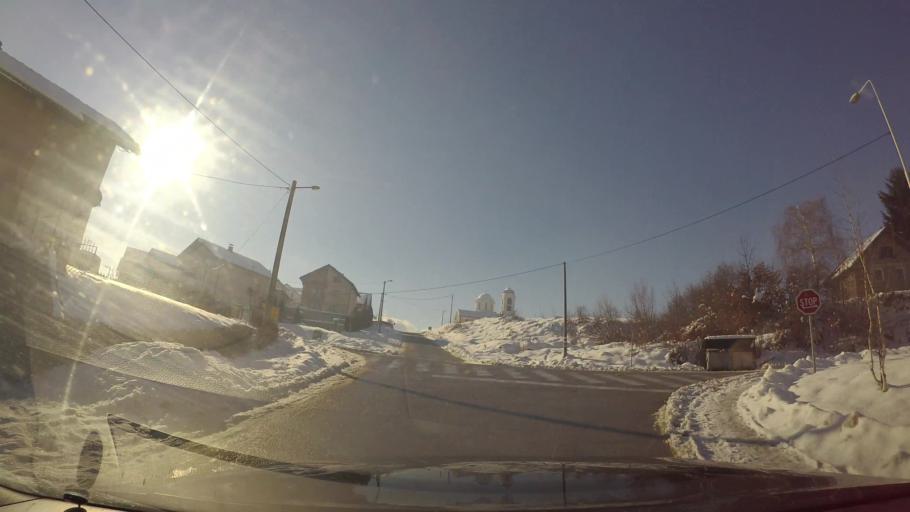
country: BA
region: Federation of Bosnia and Herzegovina
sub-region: Kanton Sarajevo
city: Sarajevo
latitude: 43.8198
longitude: 18.3714
